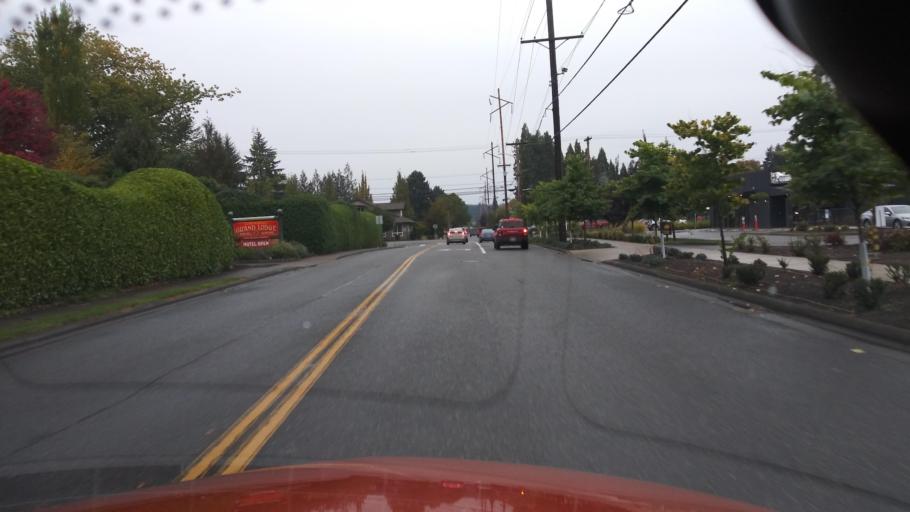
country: US
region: Oregon
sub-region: Washington County
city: Forest Grove
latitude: 45.5211
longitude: -123.0881
